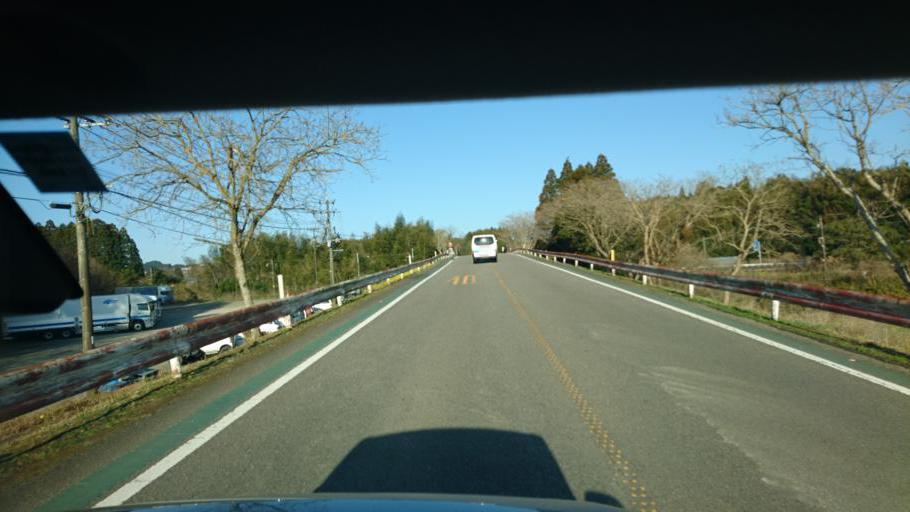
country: JP
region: Miyazaki
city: Miyazaki-shi
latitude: 31.8578
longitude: 131.3705
